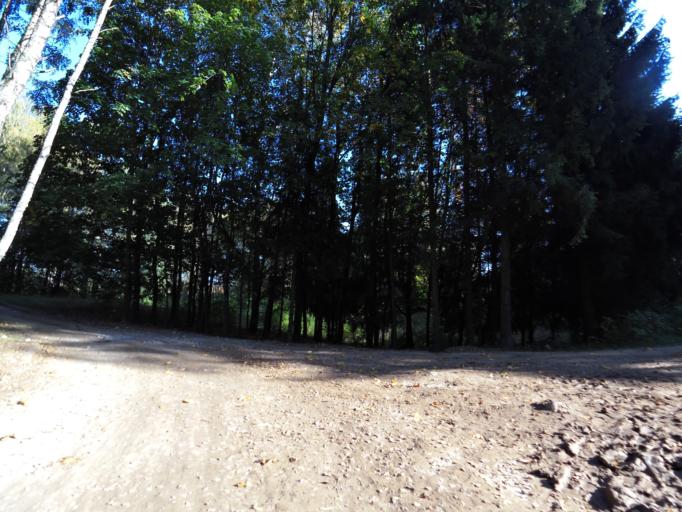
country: LT
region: Vilnius County
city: Pilaite
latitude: 54.7184
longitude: 25.1908
